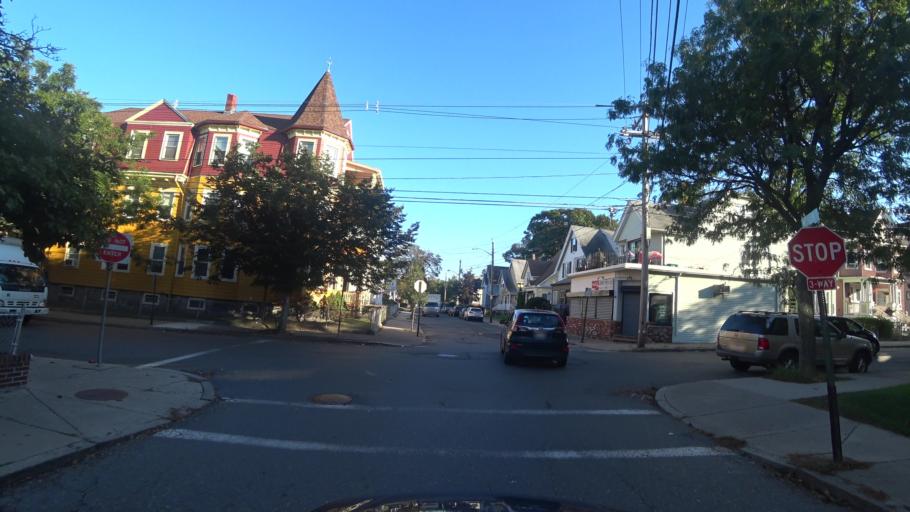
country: US
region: Massachusetts
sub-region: Middlesex County
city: Everett
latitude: 42.4141
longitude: -71.0525
